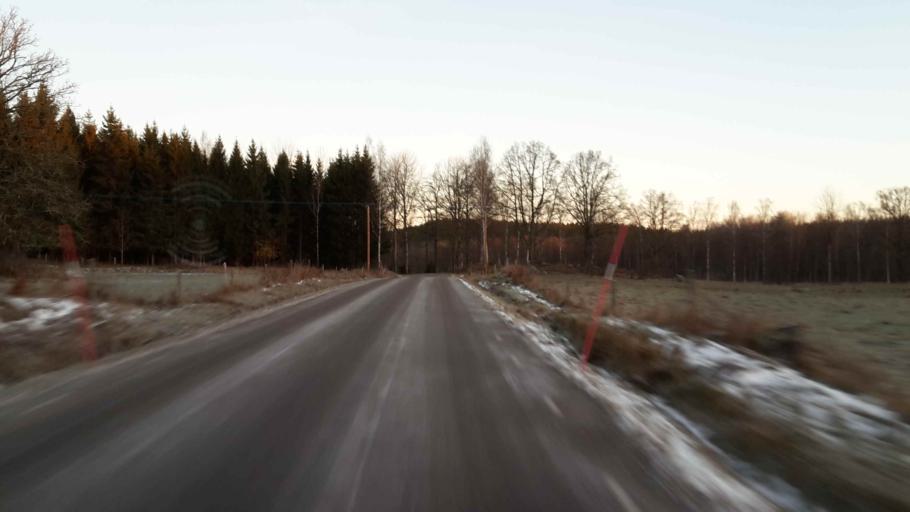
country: SE
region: OEstergoetland
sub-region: Atvidabergs Kommun
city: Atvidaberg
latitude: 58.2735
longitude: 16.1481
